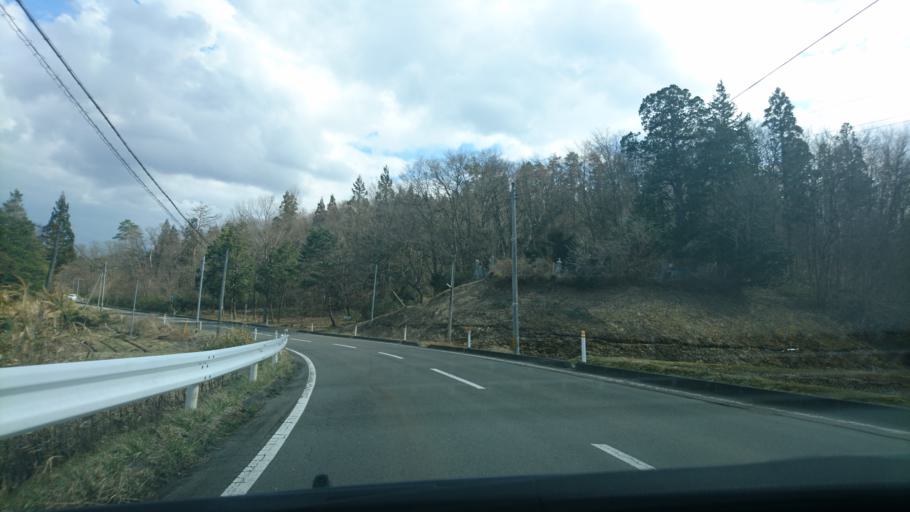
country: JP
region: Iwate
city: Hanamaki
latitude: 39.3410
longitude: 141.2359
